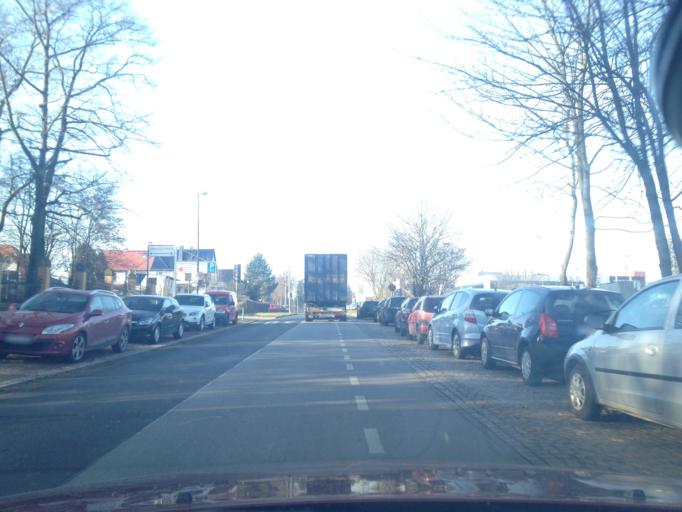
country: DE
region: Saxony
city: Goerlitz
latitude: 51.1626
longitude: 14.9700
